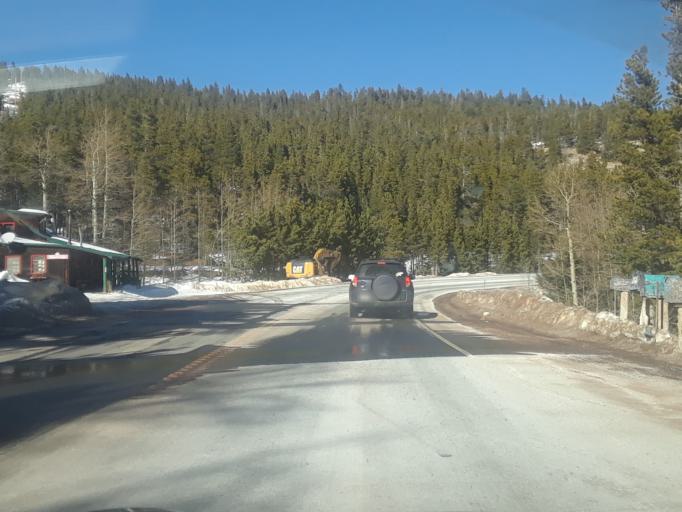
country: US
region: Colorado
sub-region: Boulder County
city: Nederland
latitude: 40.0781
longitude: -105.5024
